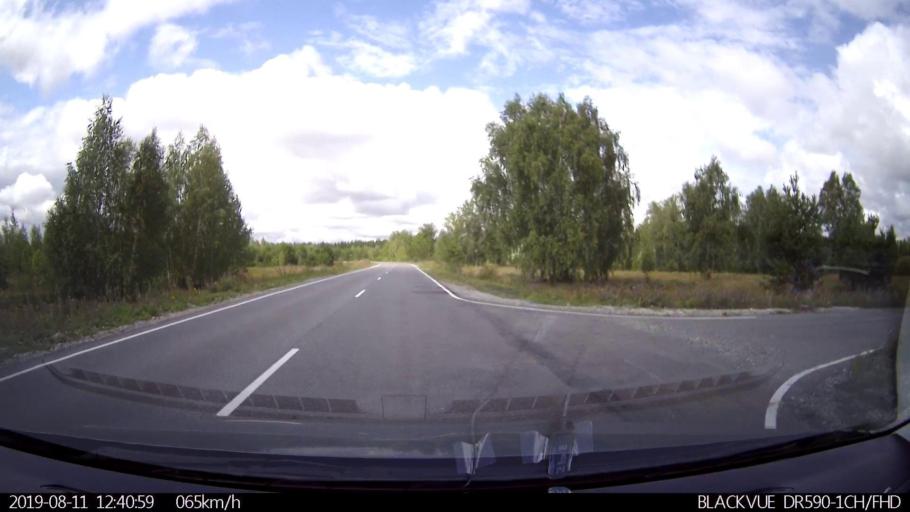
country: RU
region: Ulyanovsk
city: Ignatovka
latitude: 53.8416
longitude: 47.7731
